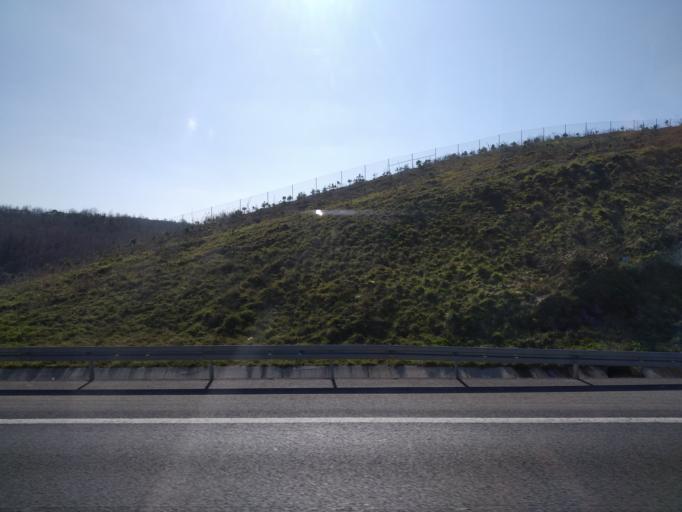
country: TR
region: Istanbul
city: Mahmut Sevket Pasa
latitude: 41.1850
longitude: 29.2206
